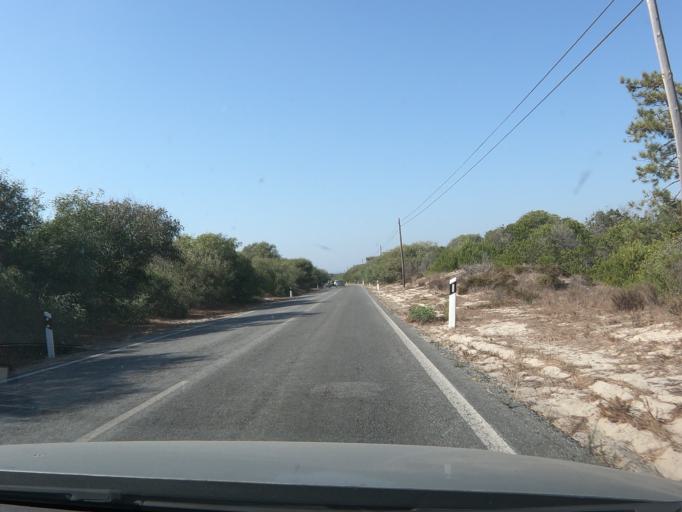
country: PT
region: Setubal
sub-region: Setubal
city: Setubal
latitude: 38.4073
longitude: -8.8105
